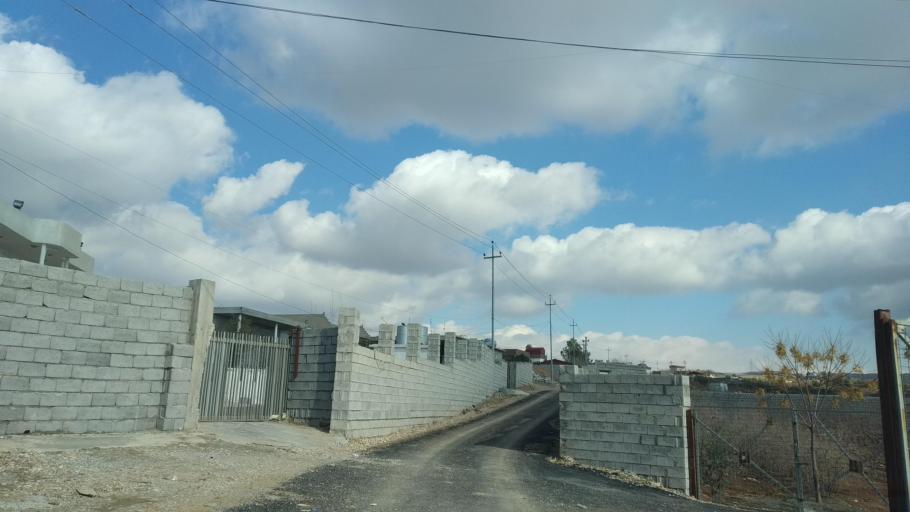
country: IQ
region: Arbil
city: Erbil
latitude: 36.2318
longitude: 44.1532
